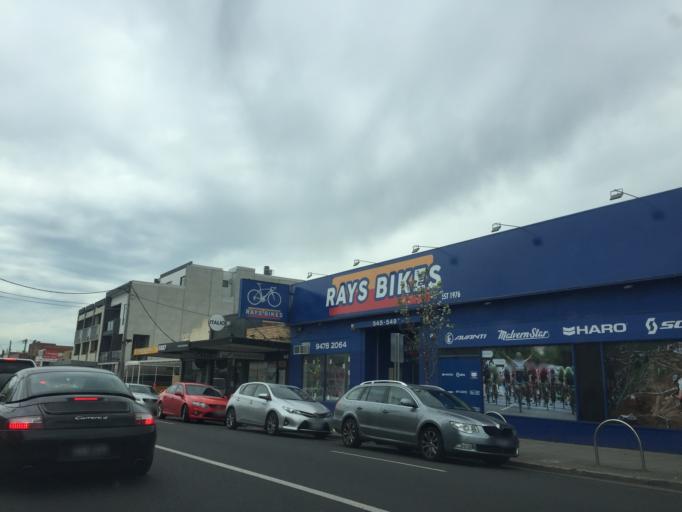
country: AU
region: Victoria
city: Thornbury
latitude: -37.7357
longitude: 145.0044
